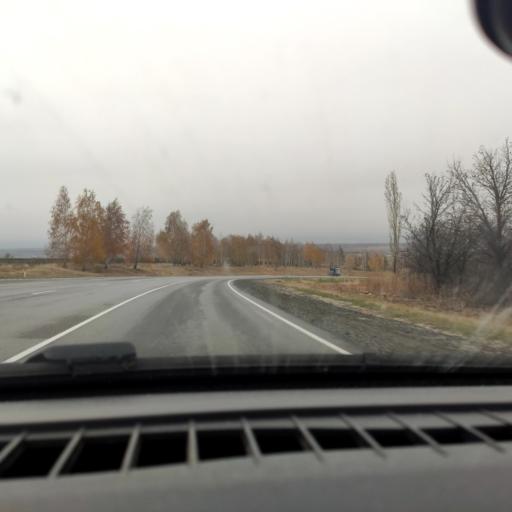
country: RU
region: Voronezj
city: Ostrogozhsk
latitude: 51.0192
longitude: 38.9820
